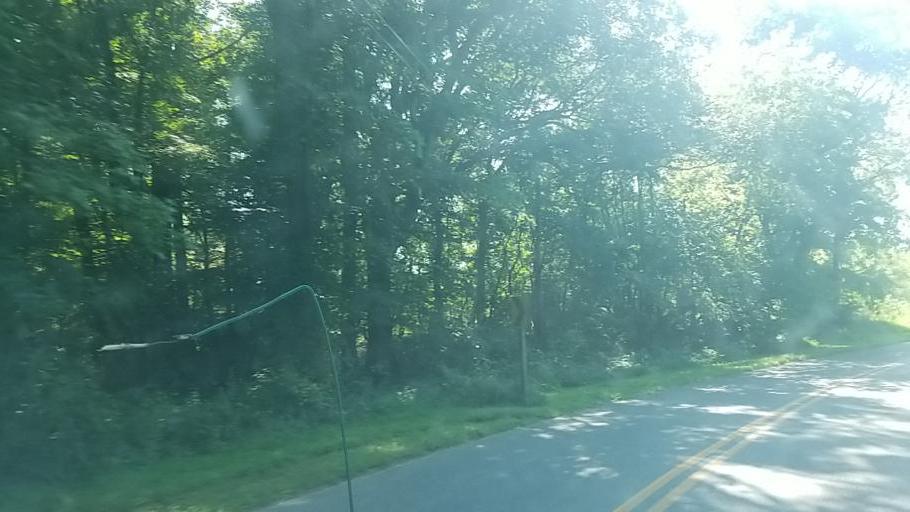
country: US
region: Maryland
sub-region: Somerset County
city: Princess Anne
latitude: 38.2598
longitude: -75.6701
